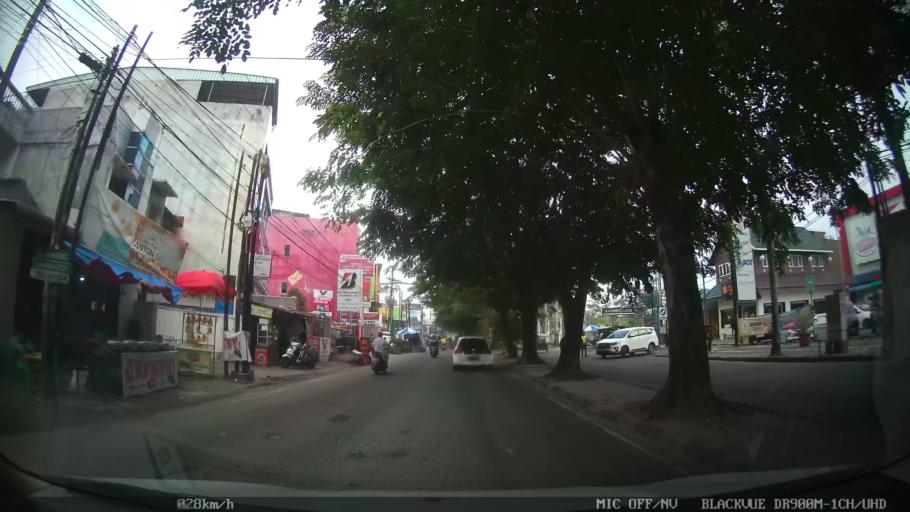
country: ID
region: North Sumatra
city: Medan
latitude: 3.5493
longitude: 98.6882
